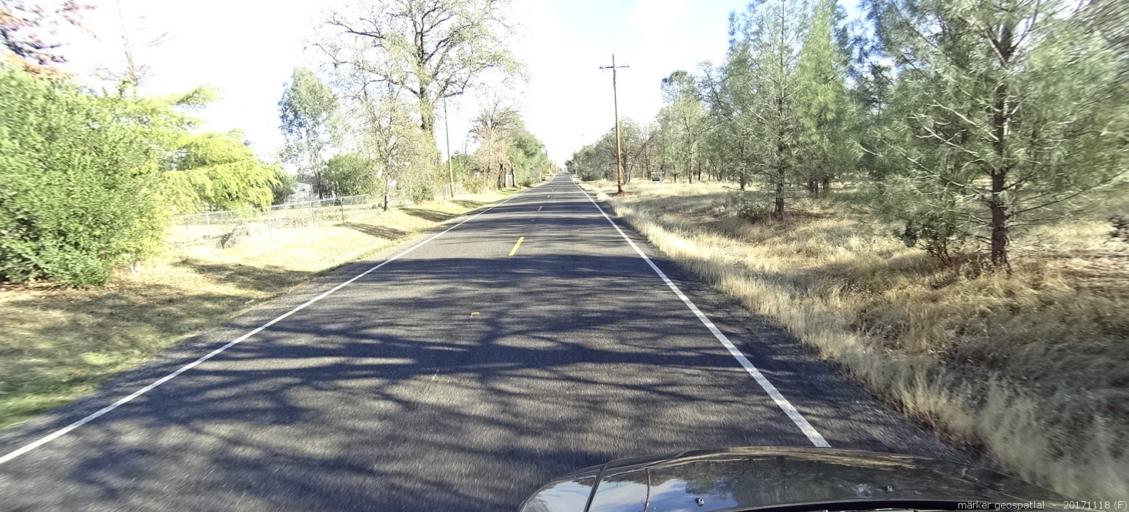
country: US
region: California
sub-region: Shasta County
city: Redding
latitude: 40.4494
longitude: -122.4489
